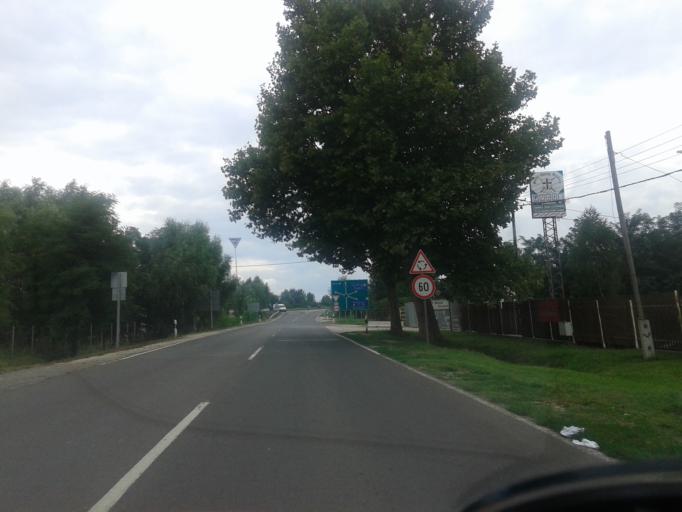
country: HU
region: Csongrad
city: Roszke
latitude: 46.1918
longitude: 20.0008
